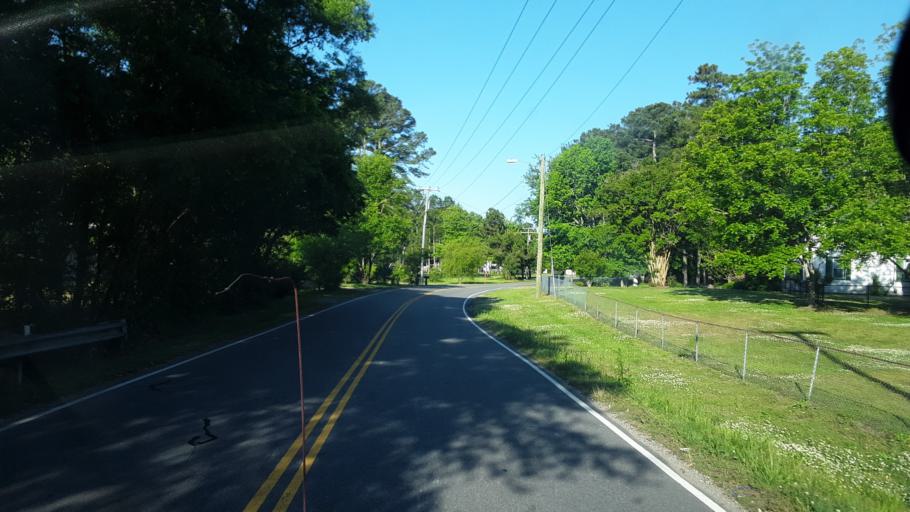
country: US
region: Virginia
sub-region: City of Virginia Beach
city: Virginia Beach
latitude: 36.7210
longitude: -76.0339
